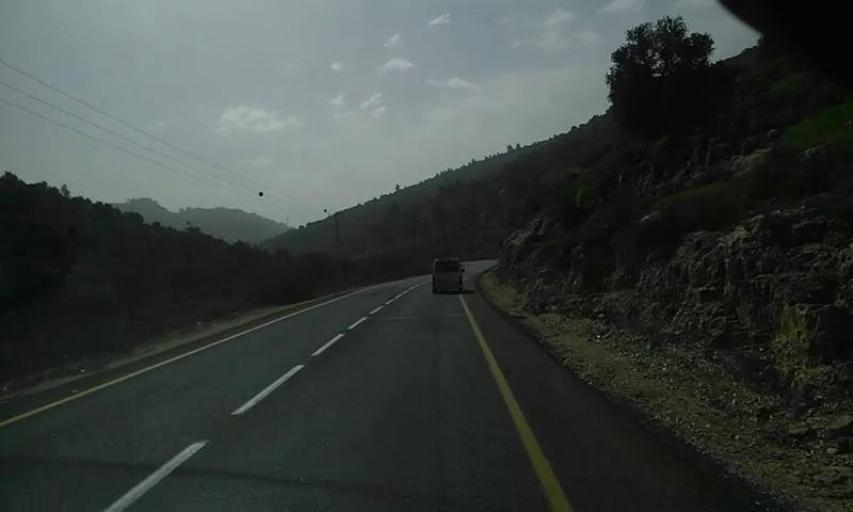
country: PS
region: West Bank
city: Silwad
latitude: 31.9966
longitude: 35.2405
